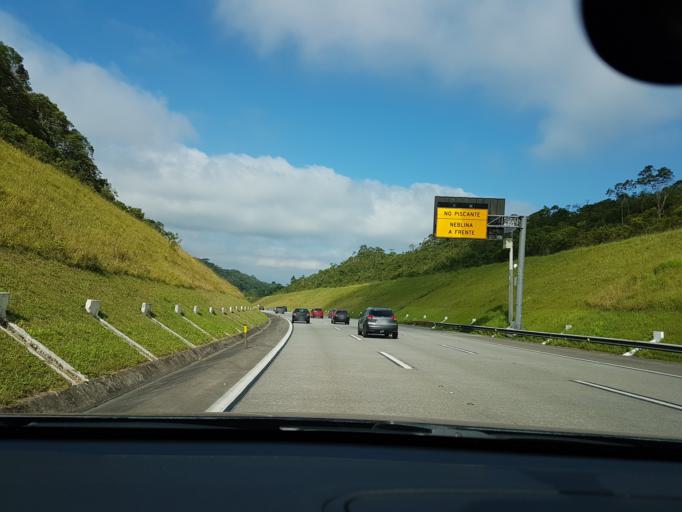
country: BR
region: Sao Paulo
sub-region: Cubatao
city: Cubatao
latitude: -23.9284
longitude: -46.5473
